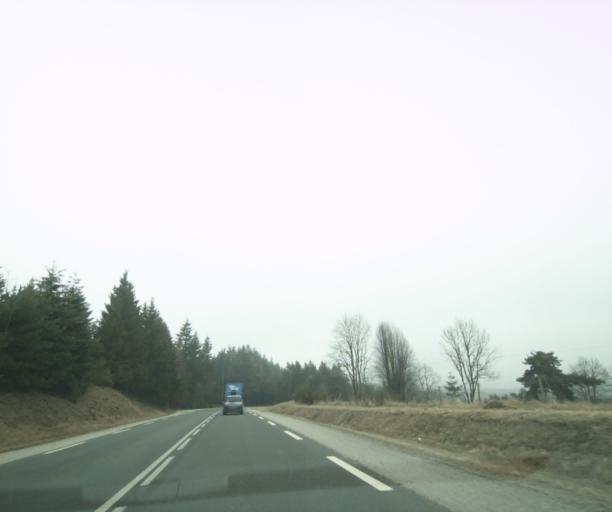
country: FR
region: Languedoc-Roussillon
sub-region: Departement de la Lozere
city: Langogne
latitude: 44.6972
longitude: 3.8164
